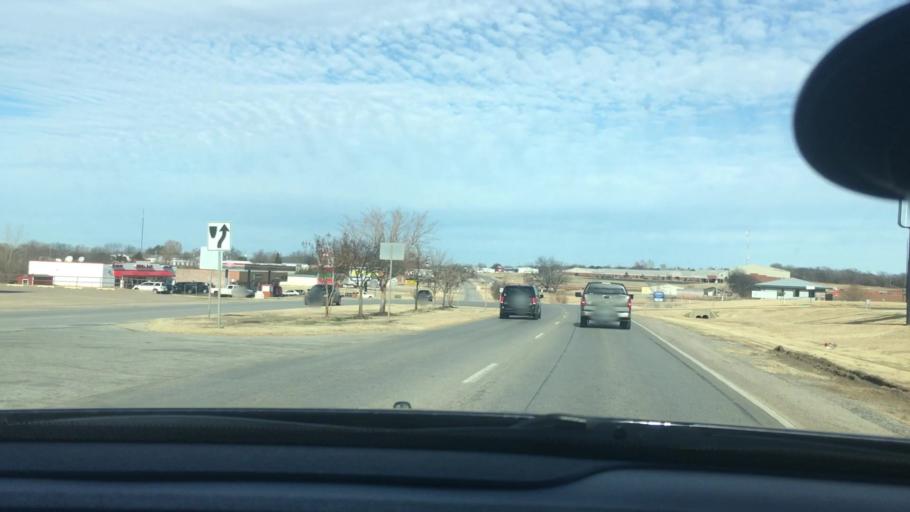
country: US
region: Oklahoma
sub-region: McClain County
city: Purcell
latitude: 35.0311
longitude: -97.3664
